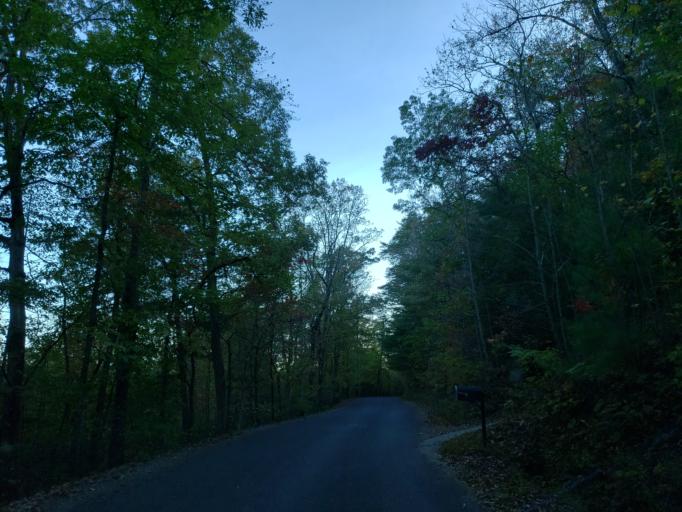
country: US
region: Georgia
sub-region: Gilmer County
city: Ellijay
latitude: 34.6470
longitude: -84.2702
